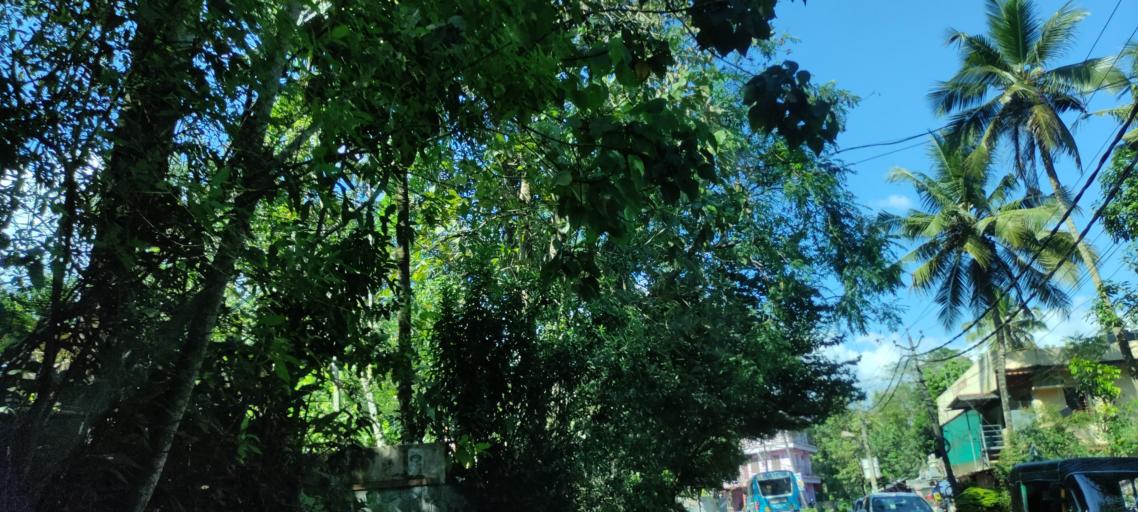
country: IN
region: Kerala
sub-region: Pattanamtitta
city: Adur
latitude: 9.1647
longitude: 76.7428
